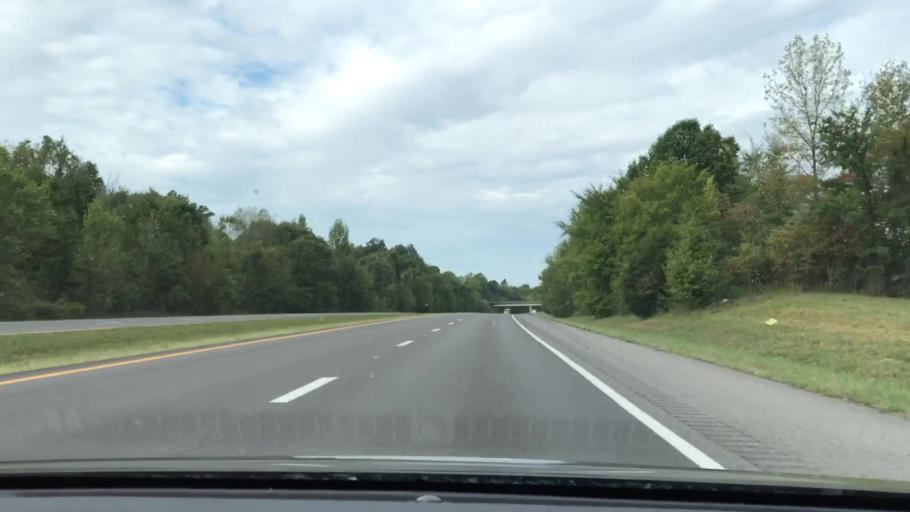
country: US
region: Kentucky
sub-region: Graves County
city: Mayfield
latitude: 36.7721
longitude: -88.6054
